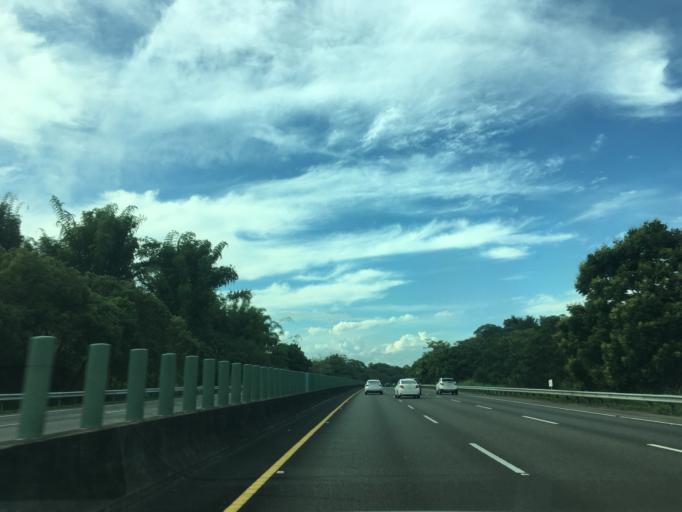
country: TW
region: Taiwan
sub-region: Chiayi
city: Jiayi Shi
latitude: 23.5640
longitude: 120.5050
